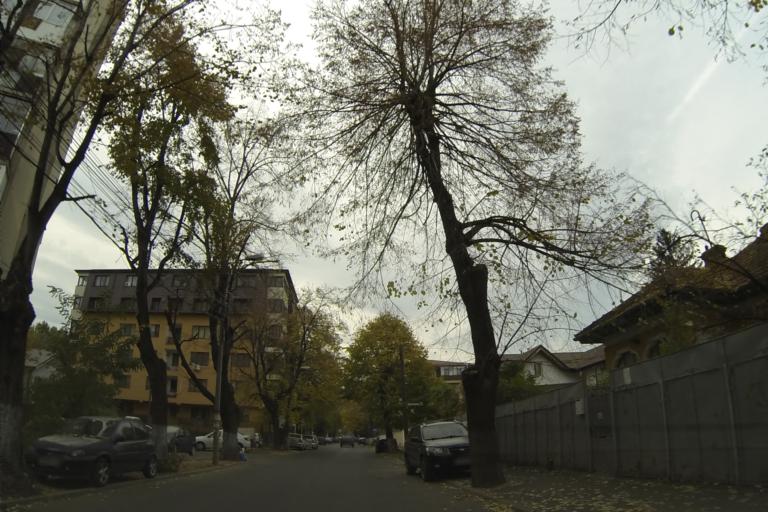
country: RO
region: Ilfov
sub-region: Comuna Chiajna
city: Rosu
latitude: 44.4352
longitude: 26.0119
